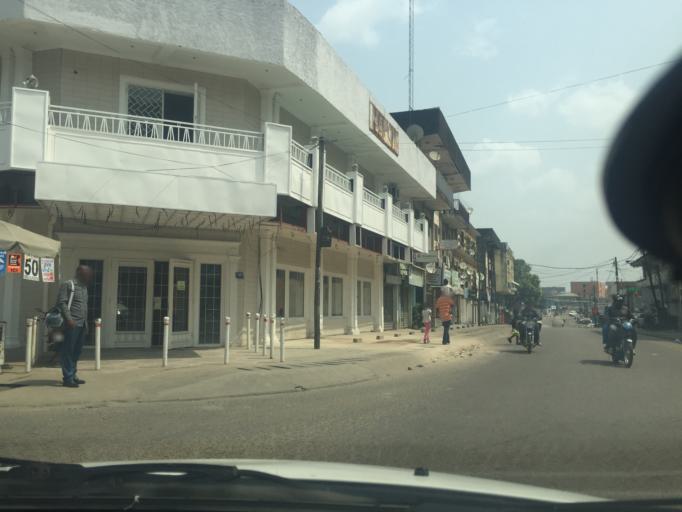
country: CM
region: Littoral
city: Douala
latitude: 4.0459
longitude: 9.6951
